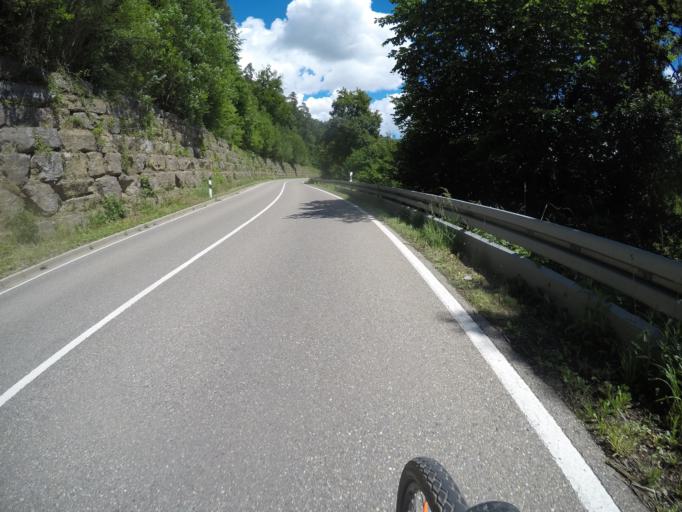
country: DE
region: Baden-Wuerttemberg
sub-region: Tuebingen Region
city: Hirrlingen
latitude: 48.4462
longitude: 8.8227
